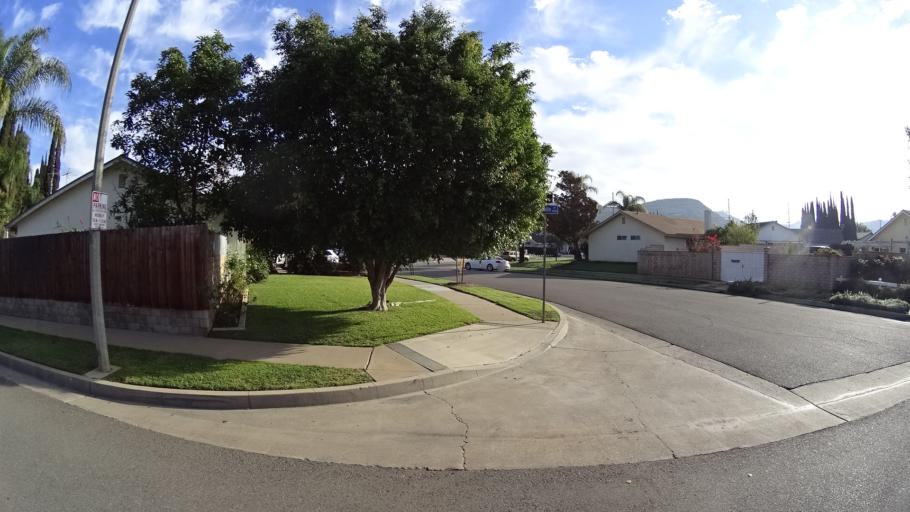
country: US
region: California
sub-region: Orange County
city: Villa Park
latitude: 33.7959
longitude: -117.8030
